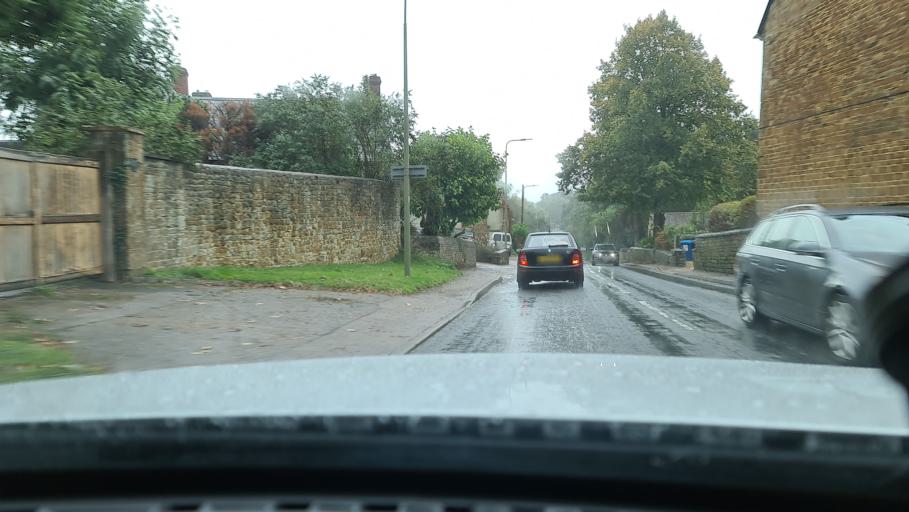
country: GB
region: England
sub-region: Oxfordshire
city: Adderbury
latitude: 52.0164
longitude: -1.3096
